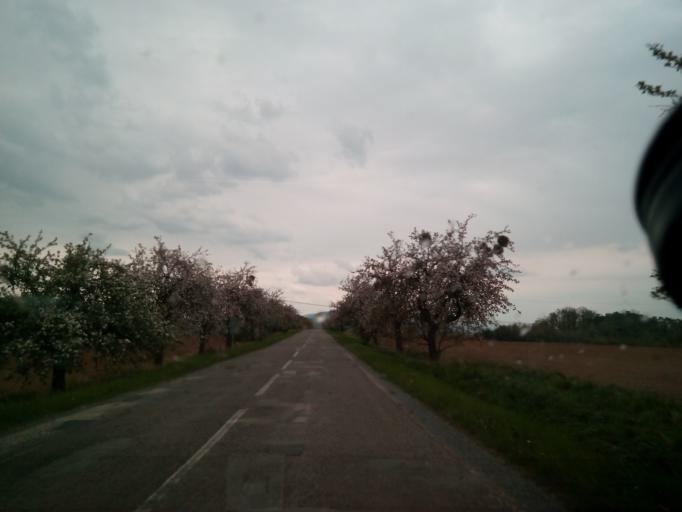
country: SK
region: Kosicky
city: Secovce
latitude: 48.7603
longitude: 21.4653
